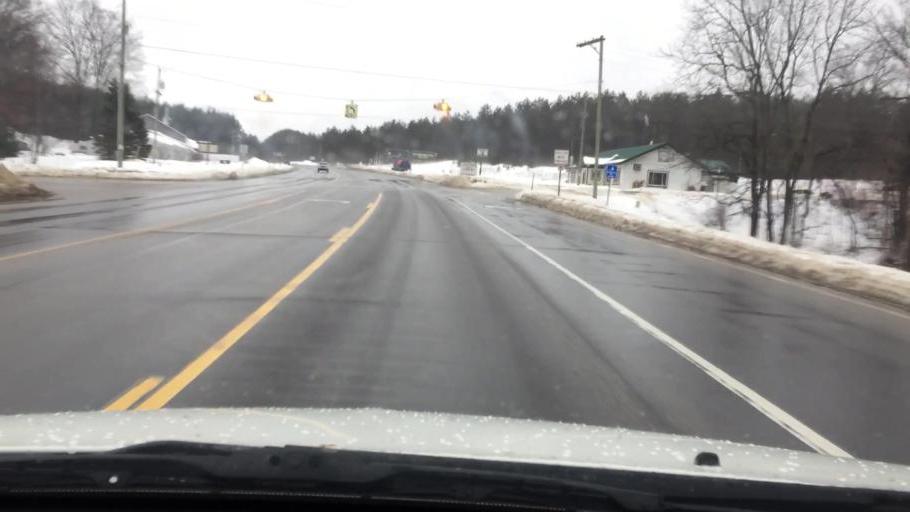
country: US
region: Michigan
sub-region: Kalkaska County
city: Kalkaska
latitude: 44.6418
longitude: -85.2859
